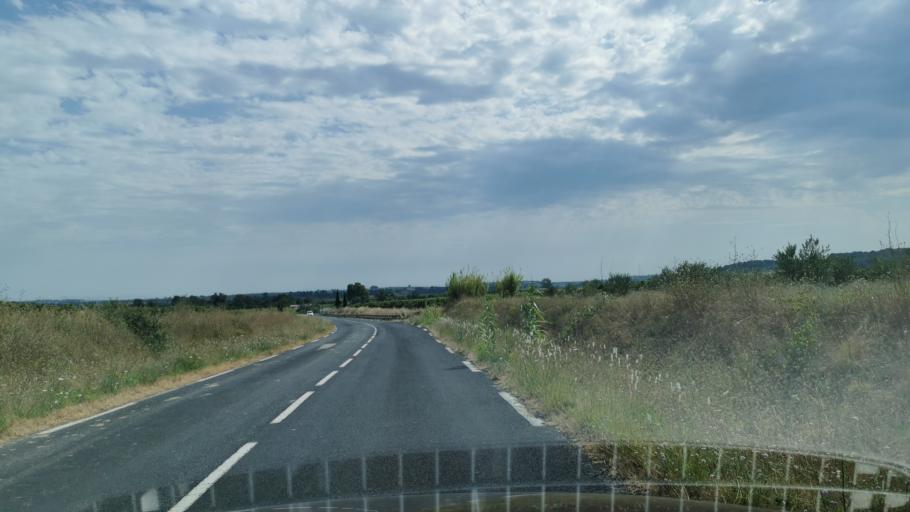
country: FR
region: Languedoc-Roussillon
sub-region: Departement de l'Herault
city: Cazouls-les-Beziers
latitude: 43.3728
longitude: 3.0961
